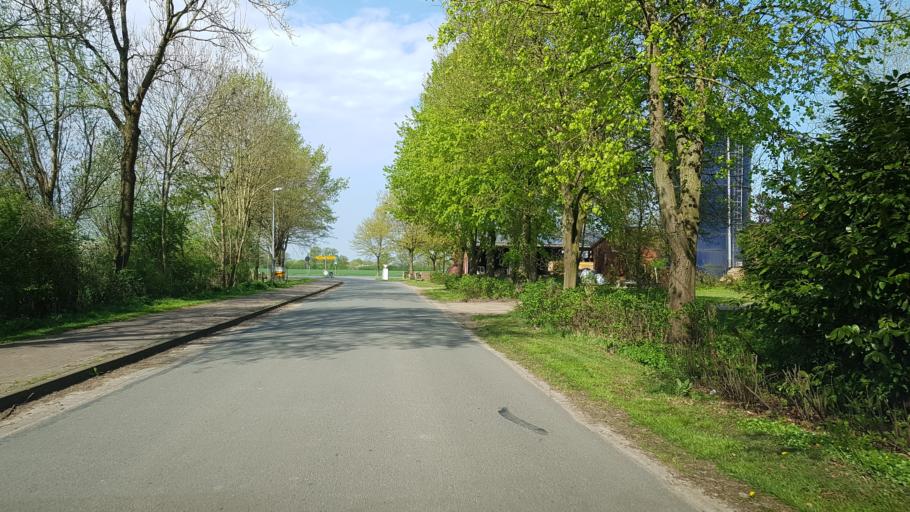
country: DE
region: Lower Saxony
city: Morsum
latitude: 52.9539
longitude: 9.0651
